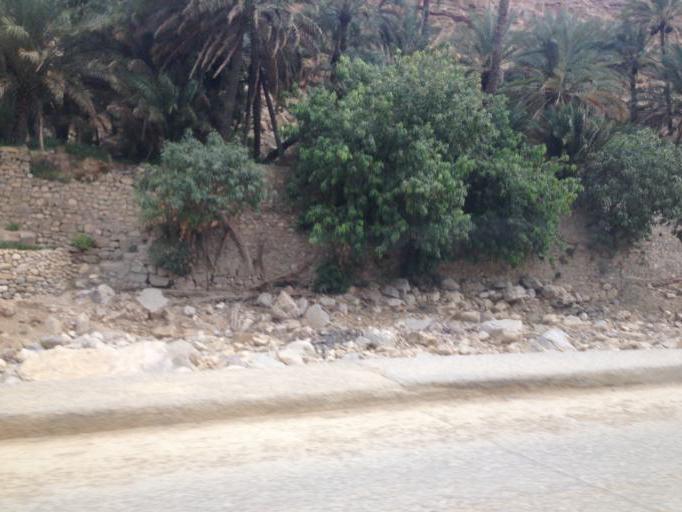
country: OM
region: Ash Sharqiyah
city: Badiyah
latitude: 22.6143
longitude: 59.0940
